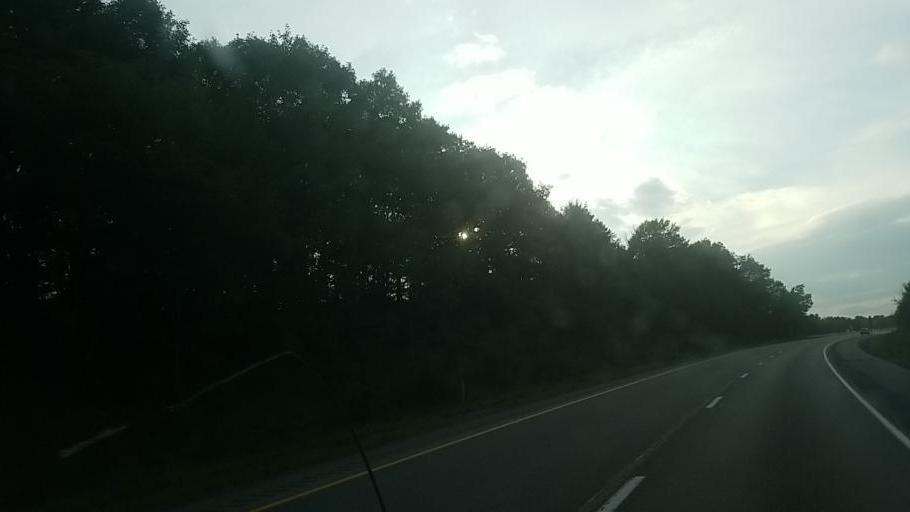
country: US
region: Pennsylvania
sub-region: Clearfield County
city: Troy
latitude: 40.9640
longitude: -78.1096
